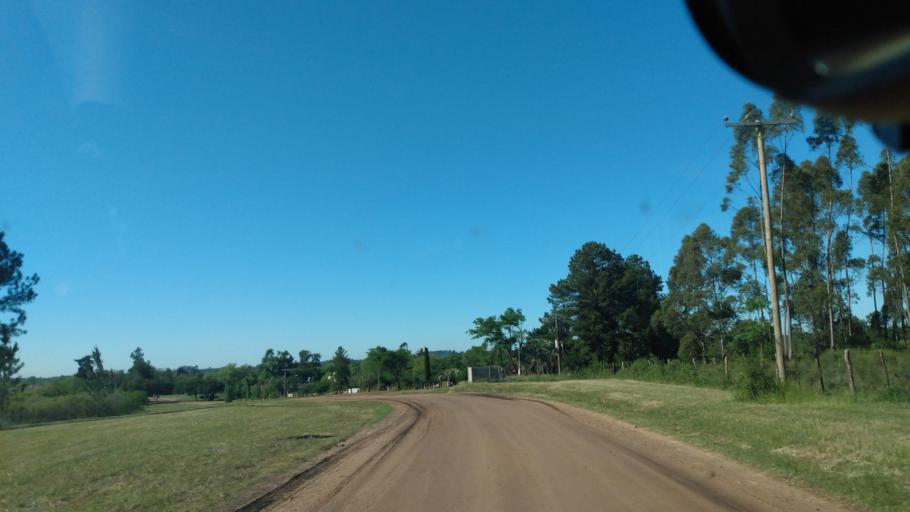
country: AR
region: Entre Rios
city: Colon
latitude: -32.1521
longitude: -58.1965
